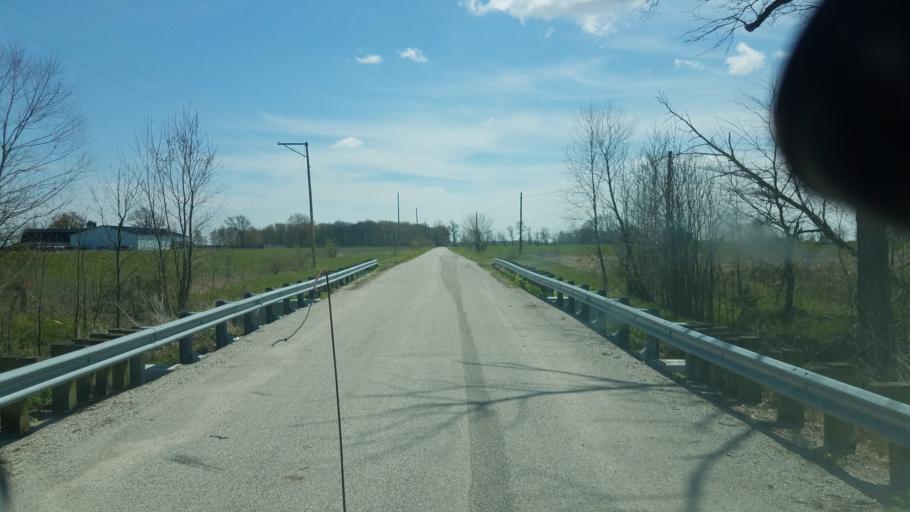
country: US
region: Ohio
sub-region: Marion County
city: Prospect
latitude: 40.4548
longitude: -83.2374
